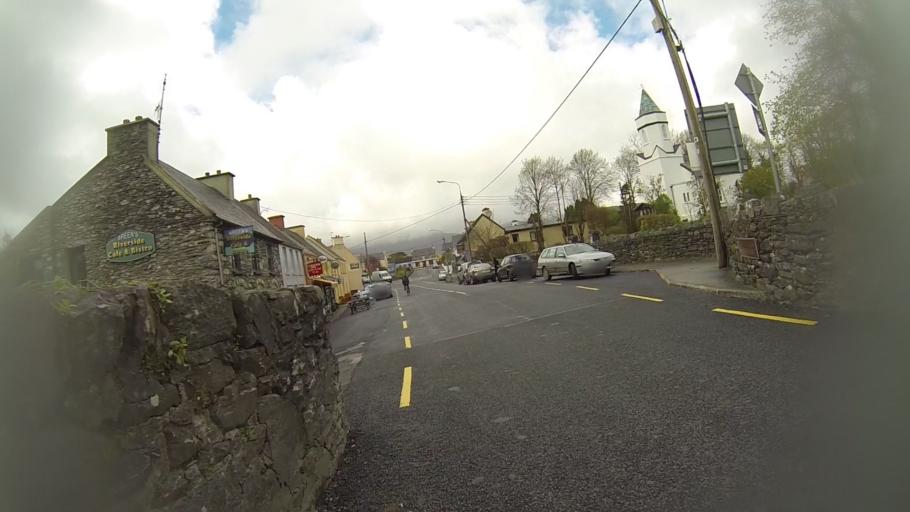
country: IE
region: Munster
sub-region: Ciarrai
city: Killorglin
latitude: 51.8383
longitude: -9.8999
